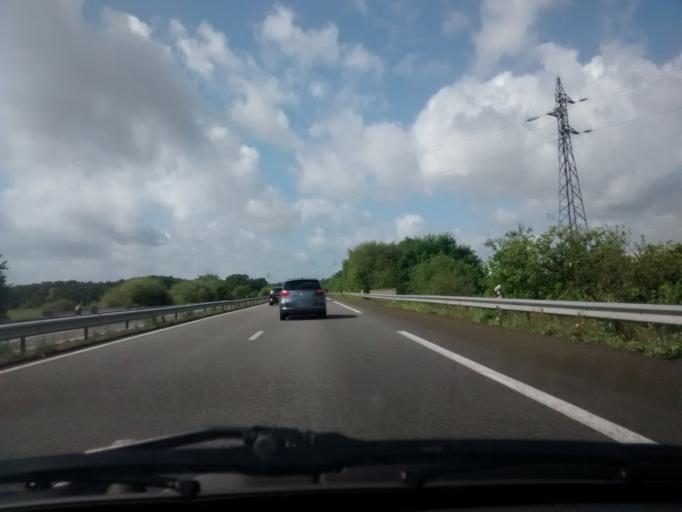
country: FR
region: Brittany
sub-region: Departement d'Ille-et-Vilaine
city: Le Rheu
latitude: 48.0860
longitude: -1.7842
